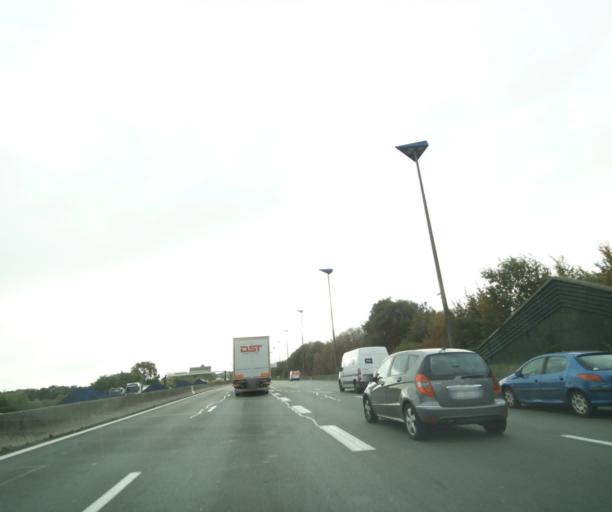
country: FR
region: Nord-Pas-de-Calais
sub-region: Departement du Nord
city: Ronchin
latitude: 50.6089
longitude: 3.0935
